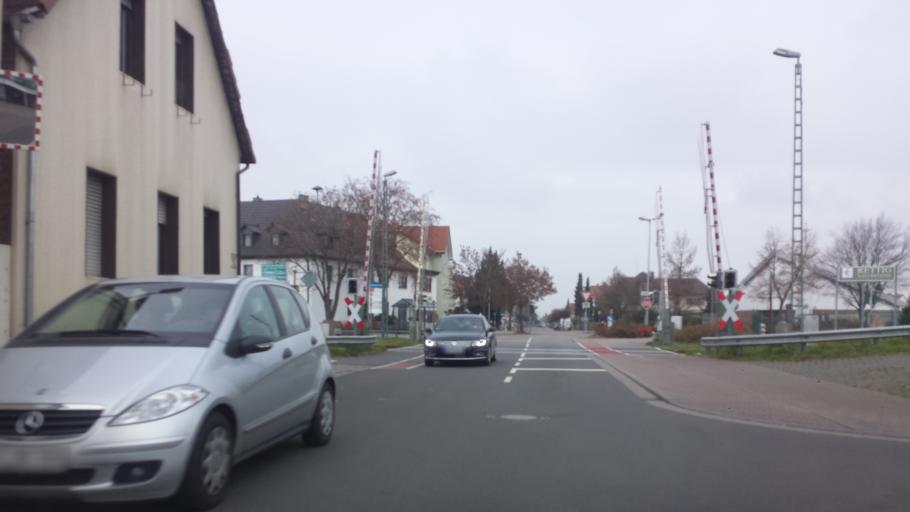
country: DE
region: Hesse
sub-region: Regierungsbezirk Darmstadt
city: Burstadt
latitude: 49.6457
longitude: 8.4542
